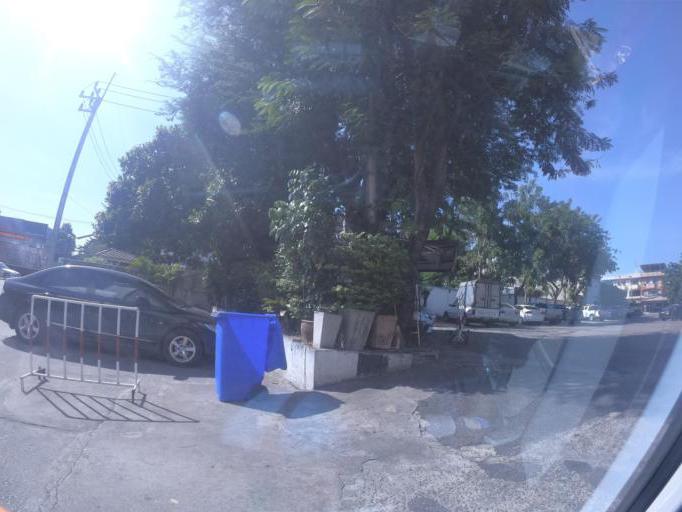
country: TH
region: Maha Sarakham
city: Chiang Yuen
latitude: 16.3741
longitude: 102.9685
